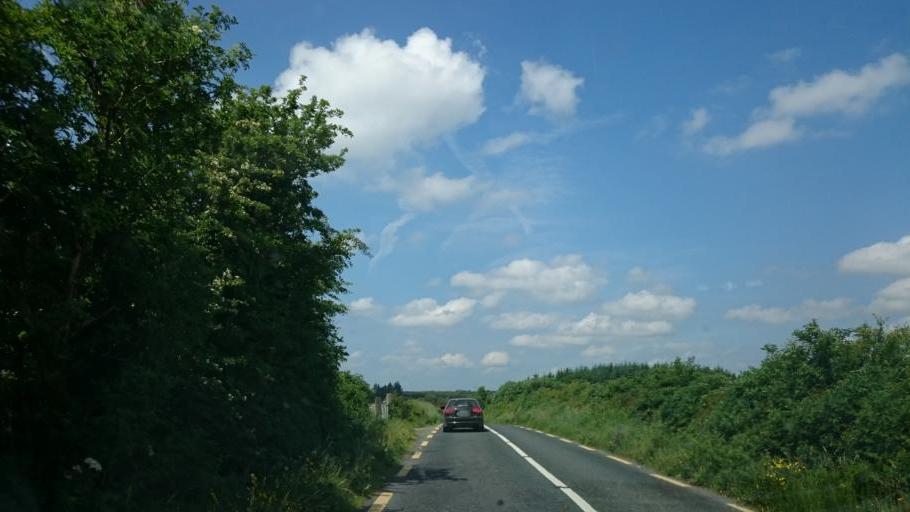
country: IE
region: Connaught
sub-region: Maigh Eo
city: Ballyhaunis
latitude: 53.8783
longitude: -8.7786
